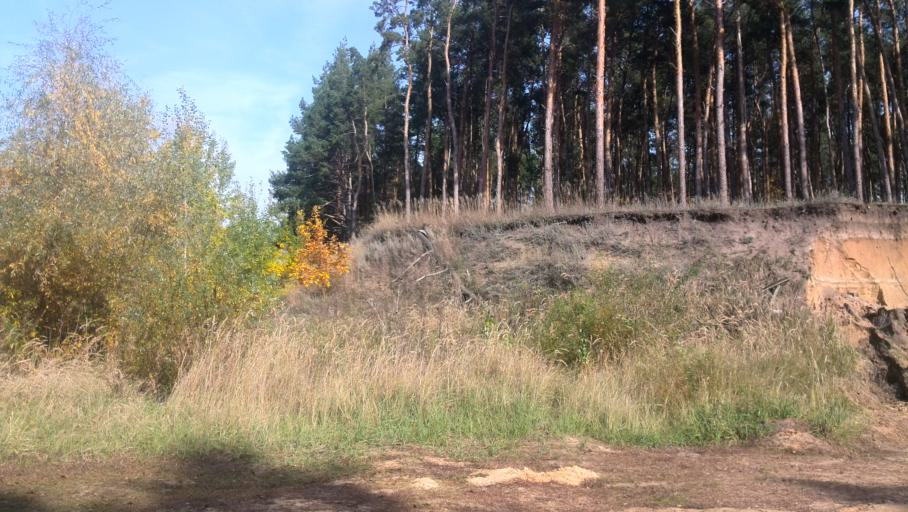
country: RU
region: Voronezj
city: Kalach
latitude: 50.4740
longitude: 41.0055
